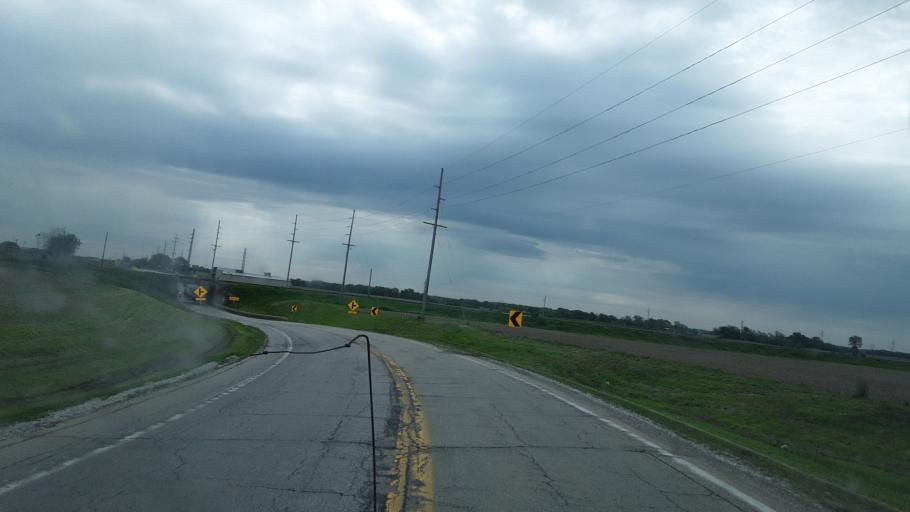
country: US
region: Illinois
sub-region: Fulton County
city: Astoria
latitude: 40.3569
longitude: -90.4246
